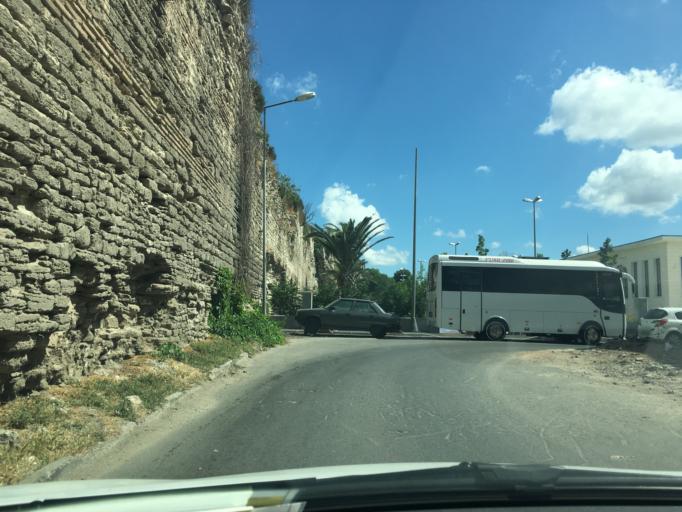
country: TR
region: Istanbul
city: Istanbul
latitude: 41.0168
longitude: 28.9230
